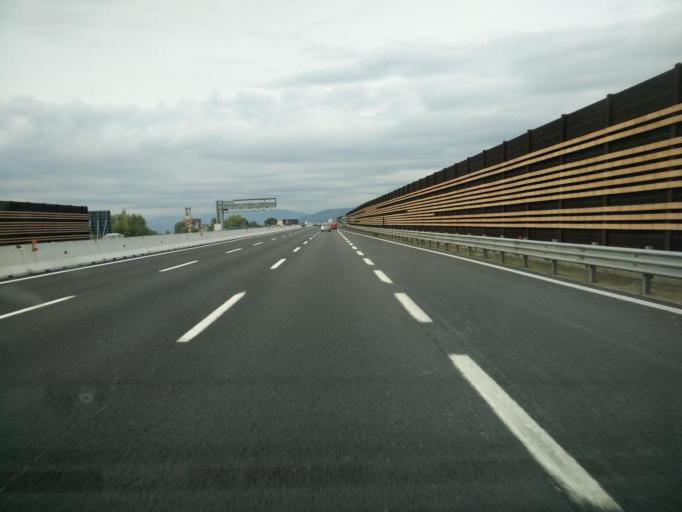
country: IT
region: Tuscany
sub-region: Province of Florence
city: Mantignano-Ugnano
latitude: 43.7811
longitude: 11.1605
